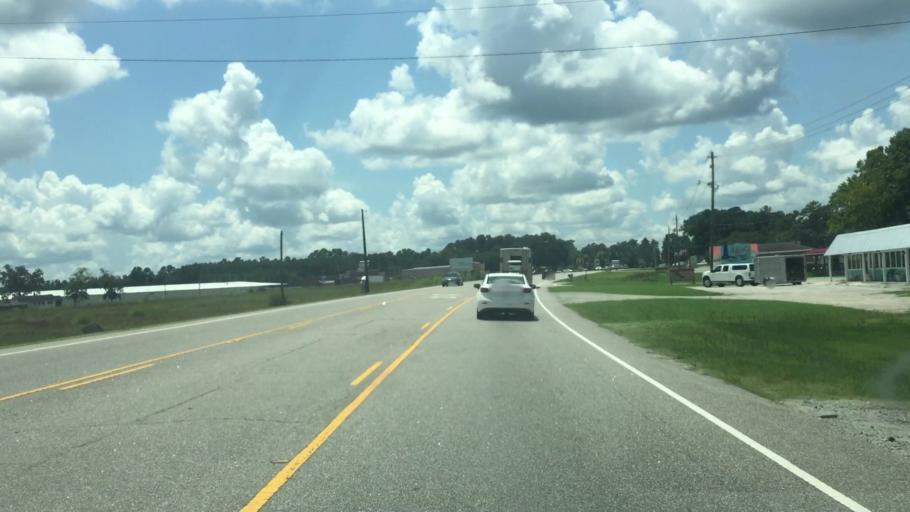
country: US
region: North Carolina
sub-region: Columbus County
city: Tabor City
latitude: 34.1432
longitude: -78.8652
